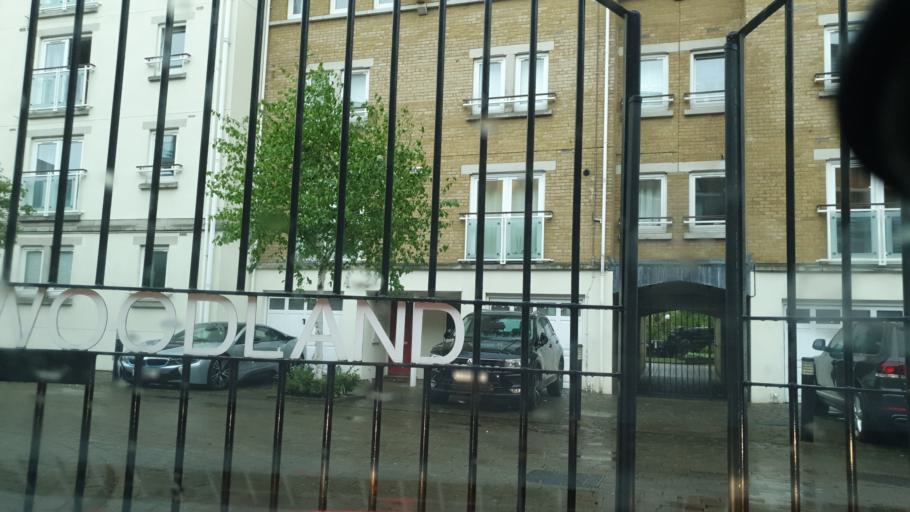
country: GB
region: England
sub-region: Greater London
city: Bethnal Green
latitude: 51.4996
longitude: -0.0479
